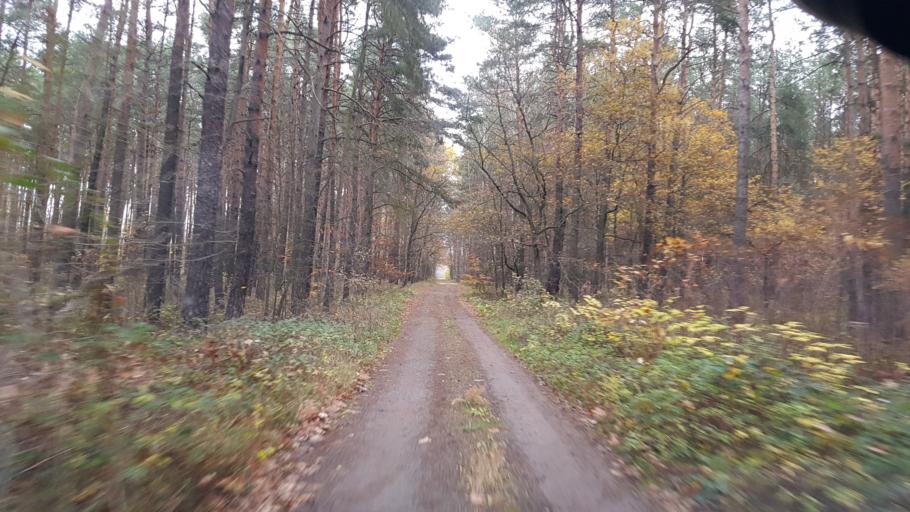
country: DE
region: Brandenburg
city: Sallgast
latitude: 51.6183
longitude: 13.8796
